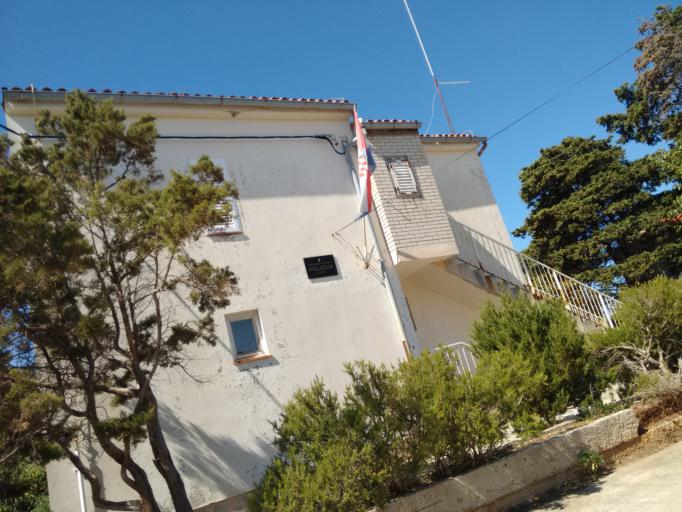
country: HR
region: Licko-Senjska
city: Novalja
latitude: 44.3760
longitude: 14.6945
